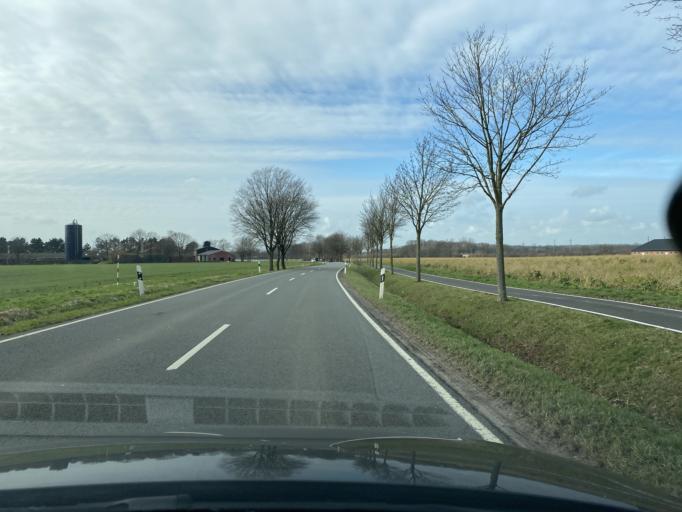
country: DE
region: North Rhine-Westphalia
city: Oelde
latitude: 51.8353
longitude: 8.1947
